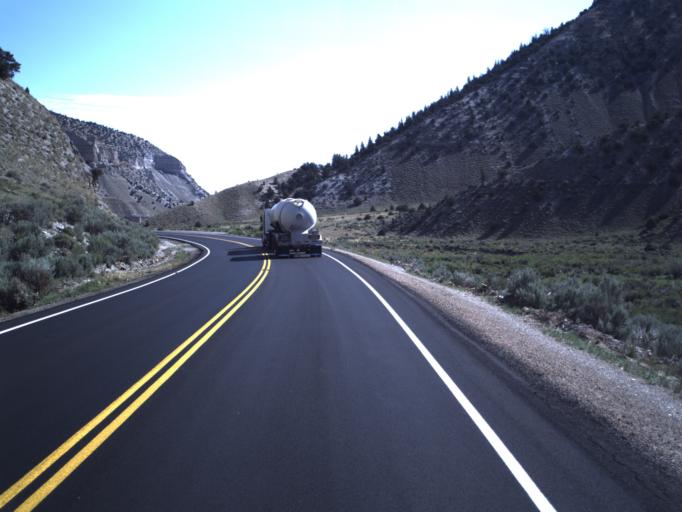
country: US
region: Utah
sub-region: Duchesne County
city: Duchesne
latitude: 39.9744
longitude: -110.6208
